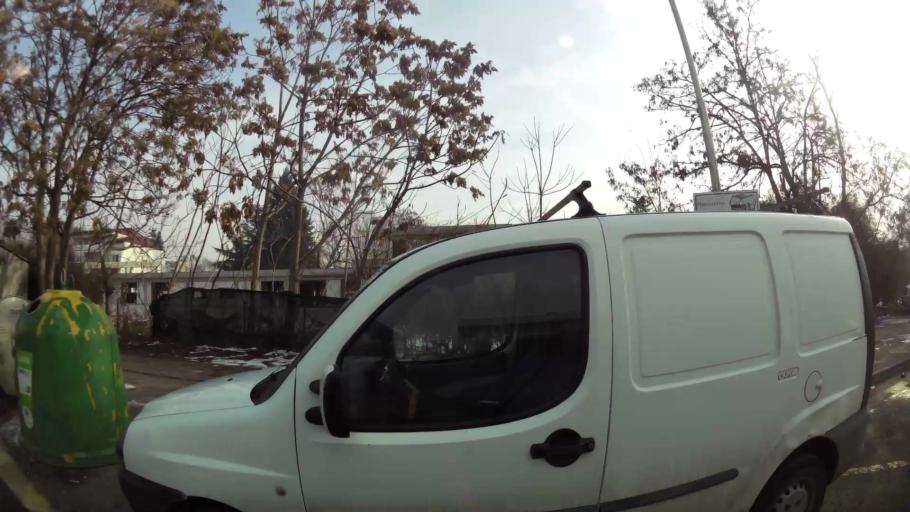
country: MK
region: Cair
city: Cair
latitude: 42.0229
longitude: 21.4342
